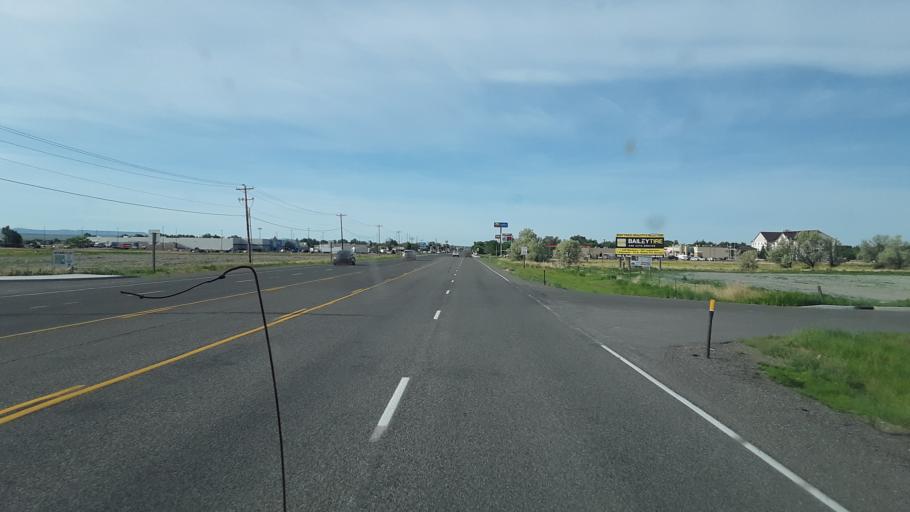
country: US
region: Wyoming
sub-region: Fremont County
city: Riverton
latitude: 43.0481
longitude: -108.3808
